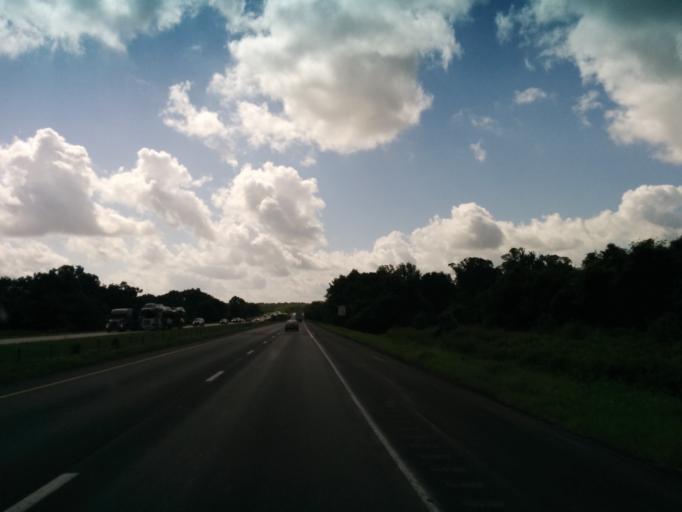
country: US
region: Texas
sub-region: Fayette County
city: Schulenburg
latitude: 29.6913
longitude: -96.8419
